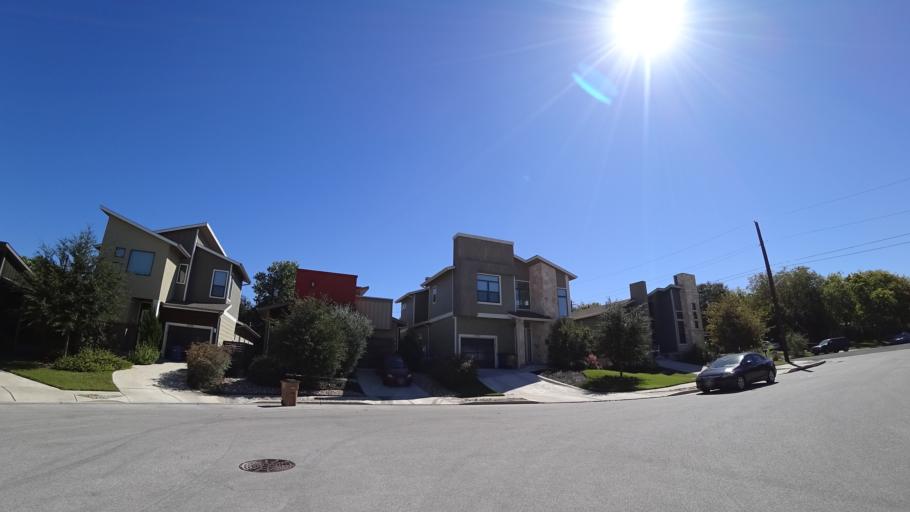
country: US
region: Texas
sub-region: Travis County
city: Austin
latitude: 30.2332
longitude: -97.7707
